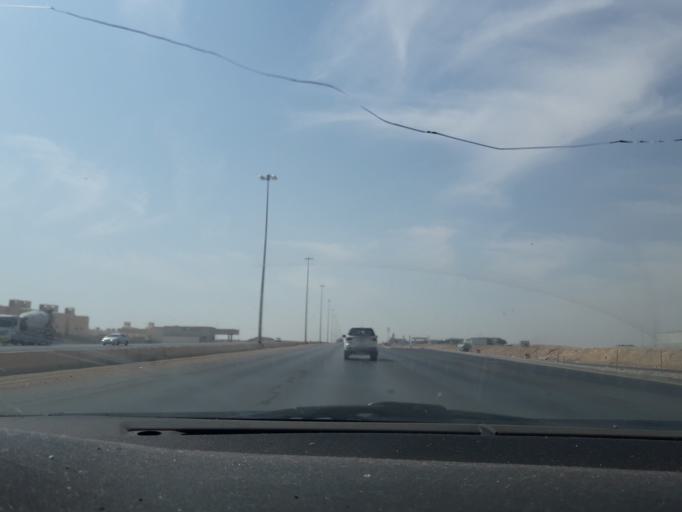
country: SA
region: Ar Riyad
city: shokhaib
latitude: 24.5509
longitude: 46.4841
